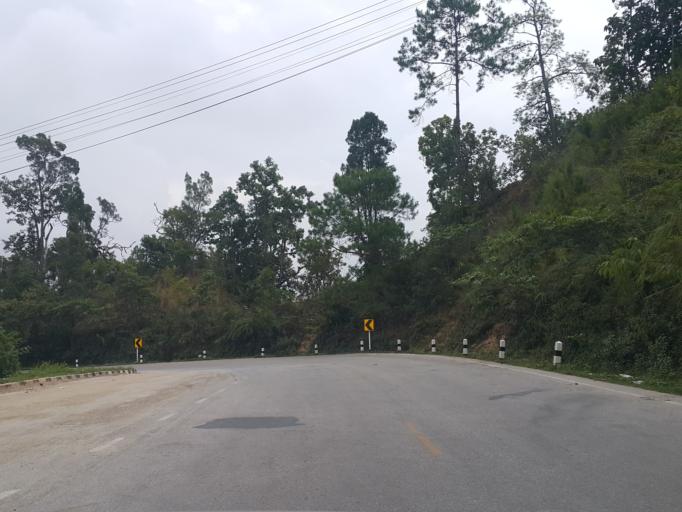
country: TH
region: Mae Hong Son
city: Mae Hi
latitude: 19.2688
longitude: 98.5227
